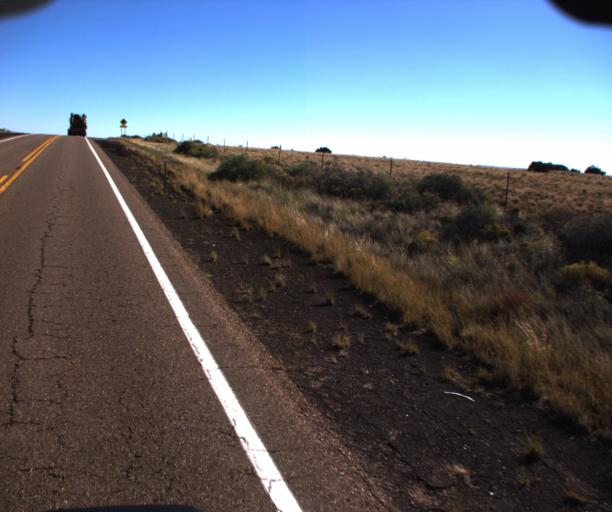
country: US
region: Arizona
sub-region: Apache County
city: Saint Johns
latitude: 34.4980
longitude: -109.5048
